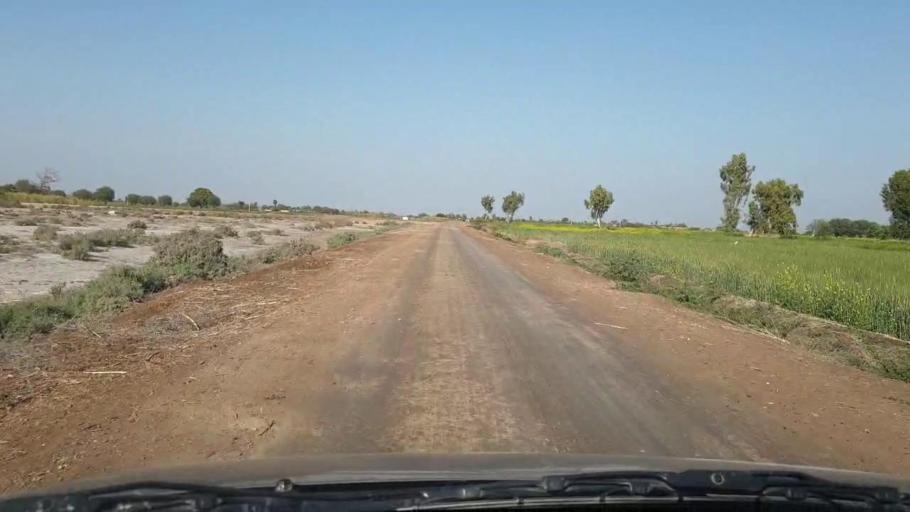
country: PK
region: Sindh
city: Samaro
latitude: 25.1650
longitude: 69.2828
